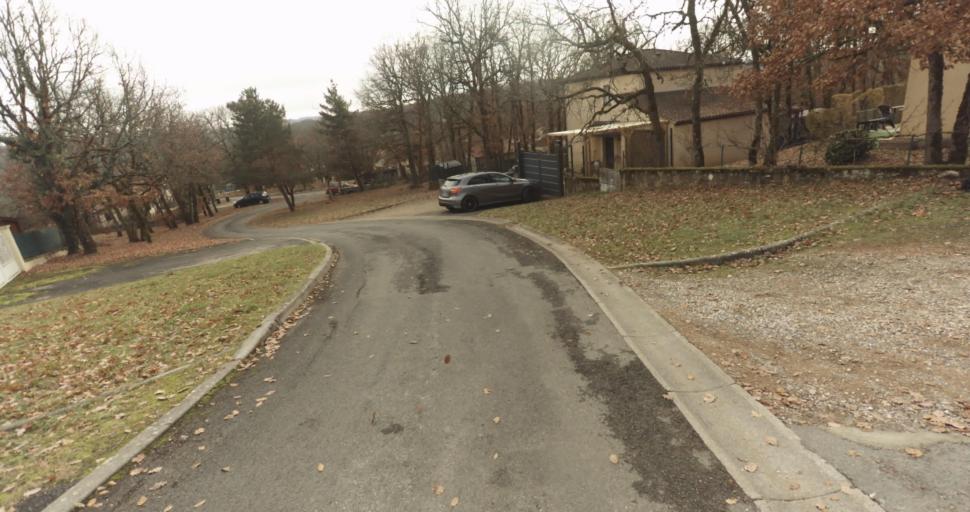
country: FR
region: Midi-Pyrenees
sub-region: Departement du Lot
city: Figeac
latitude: 44.6097
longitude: 2.0088
